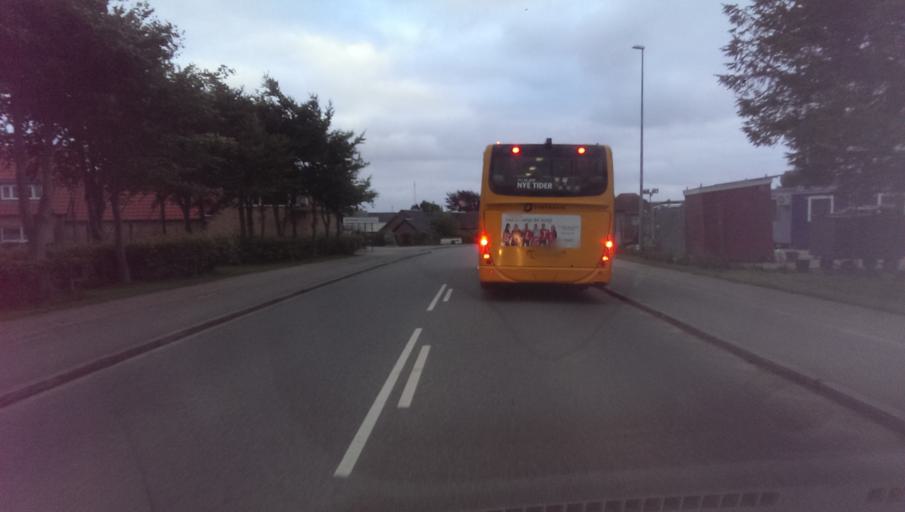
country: DK
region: South Denmark
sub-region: Esbjerg Kommune
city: Esbjerg
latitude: 55.4857
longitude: 8.4735
